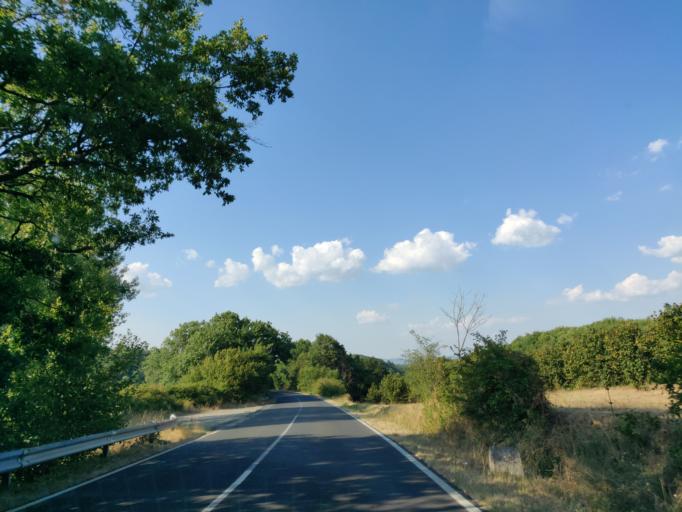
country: IT
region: Latium
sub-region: Provincia di Viterbo
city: Gradoli
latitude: 42.6452
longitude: 11.8400
